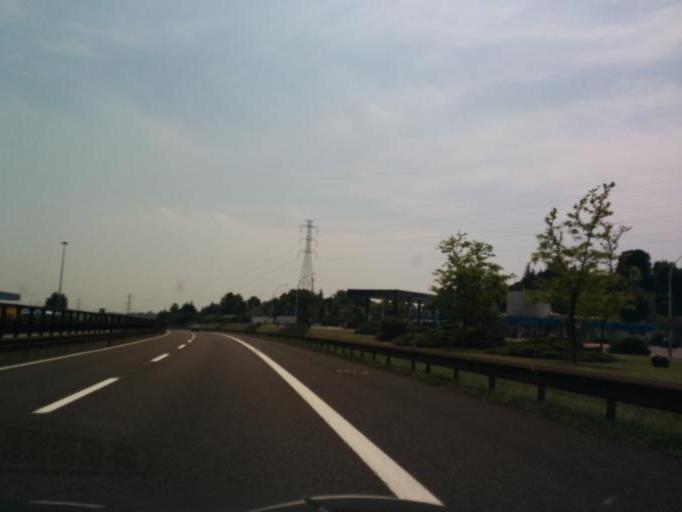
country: IT
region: Veneto
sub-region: Provincia di Verona
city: Cavajon Veronese
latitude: 45.5415
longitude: 10.7805
